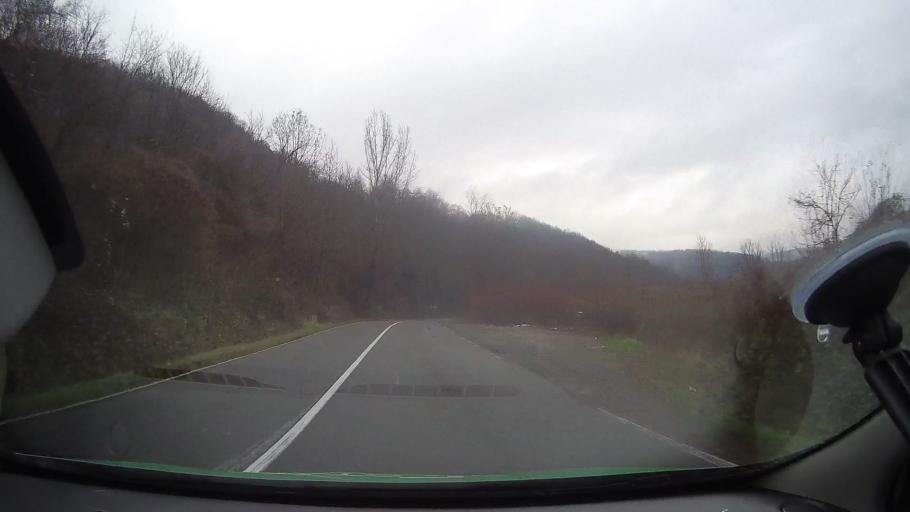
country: RO
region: Arad
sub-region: Comuna Gurahont
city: Gurahont
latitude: 46.2803
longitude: 22.3759
